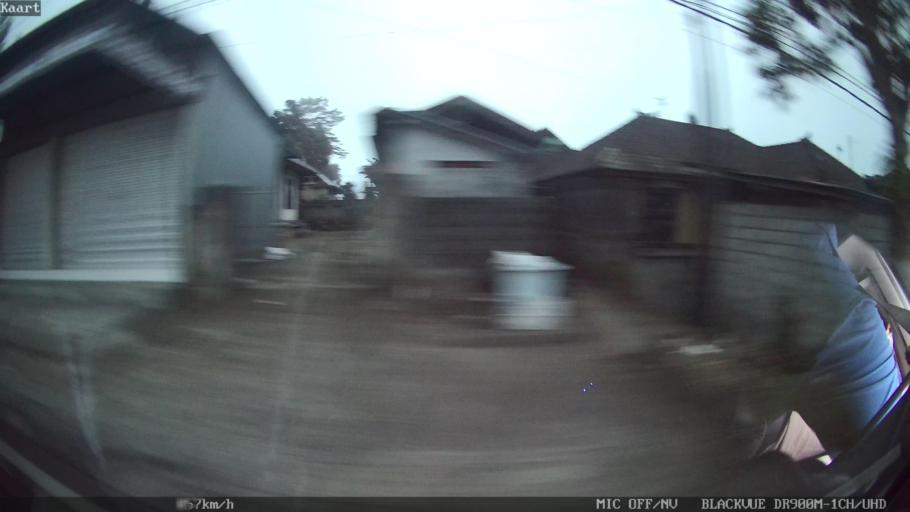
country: ID
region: Bali
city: Banjar Kedisan
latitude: -8.3045
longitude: 115.3072
